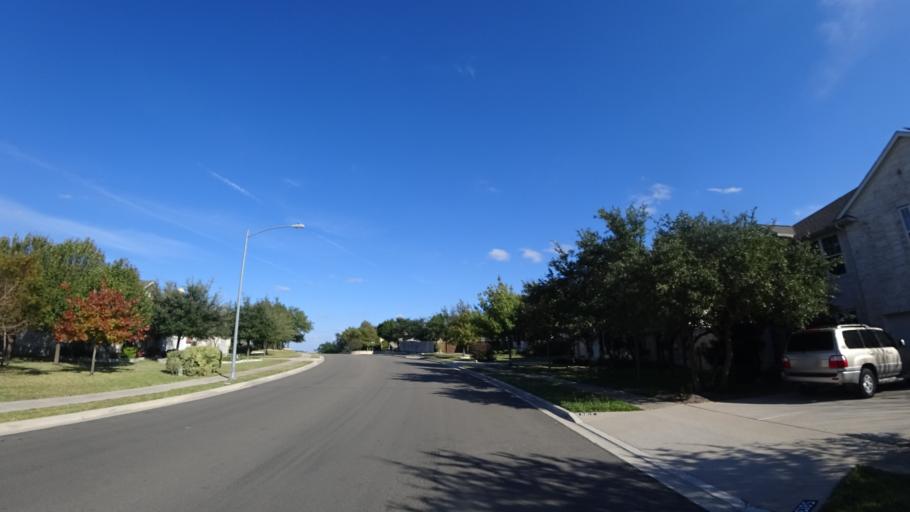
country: US
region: Texas
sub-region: Travis County
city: Barton Creek
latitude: 30.2469
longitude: -97.8721
